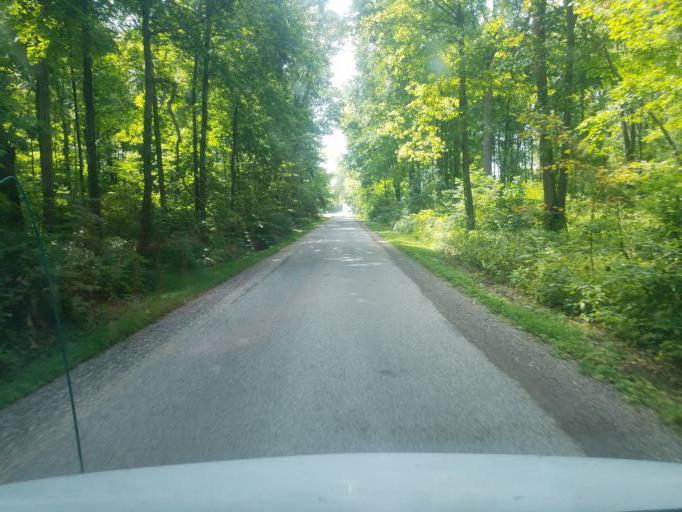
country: US
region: Ohio
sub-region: Marion County
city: Marion
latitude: 40.5071
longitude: -83.1175
